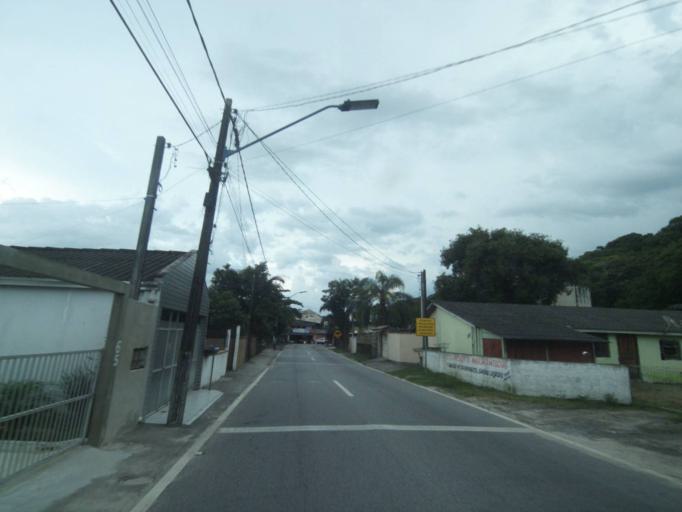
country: BR
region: Parana
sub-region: Guaratuba
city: Guaratuba
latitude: -25.8181
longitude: -48.5415
